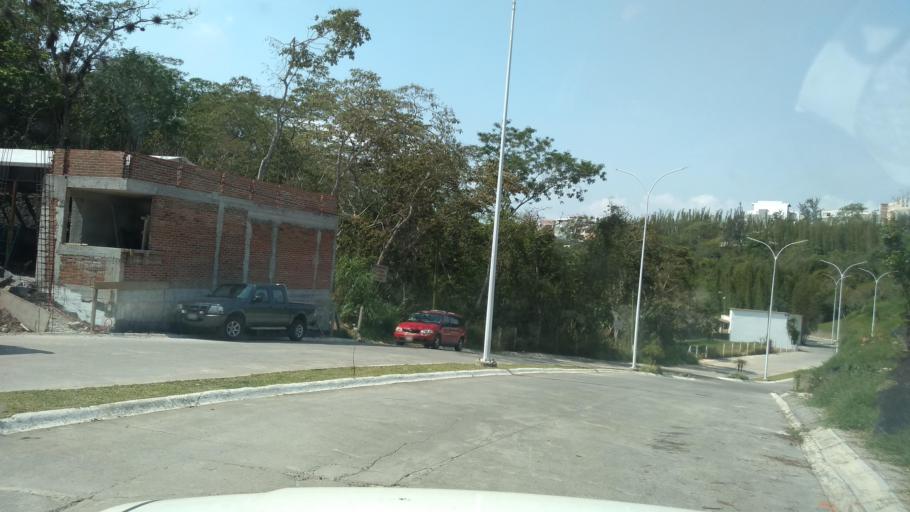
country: MX
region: Veracruz
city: El Castillo
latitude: 19.5261
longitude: -96.8626
